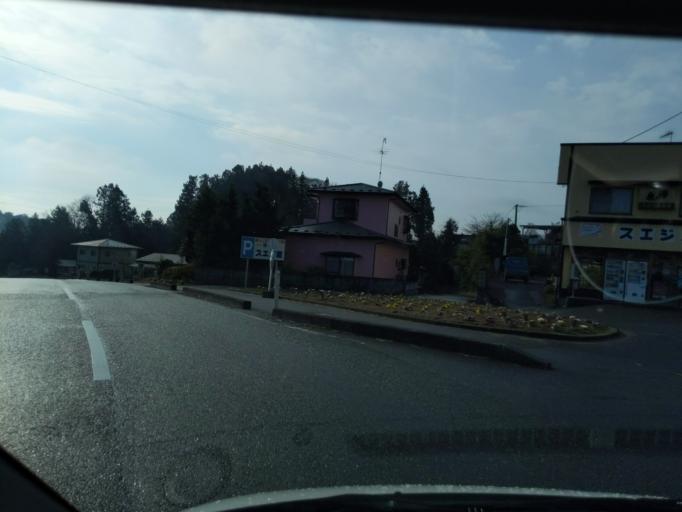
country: JP
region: Miyagi
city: Wakuya
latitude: 38.7006
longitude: 141.1594
